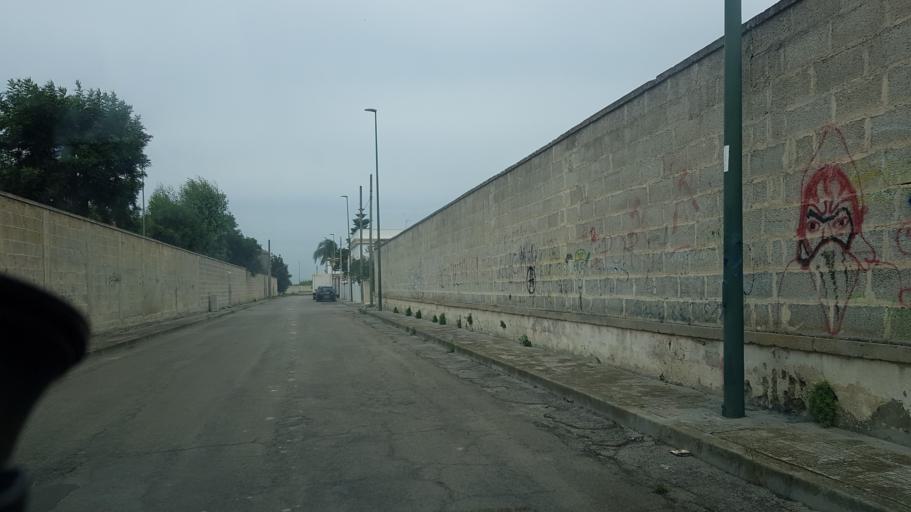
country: IT
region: Apulia
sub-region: Provincia di Lecce
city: Guagnano
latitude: 40.4023
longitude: 17.9413
